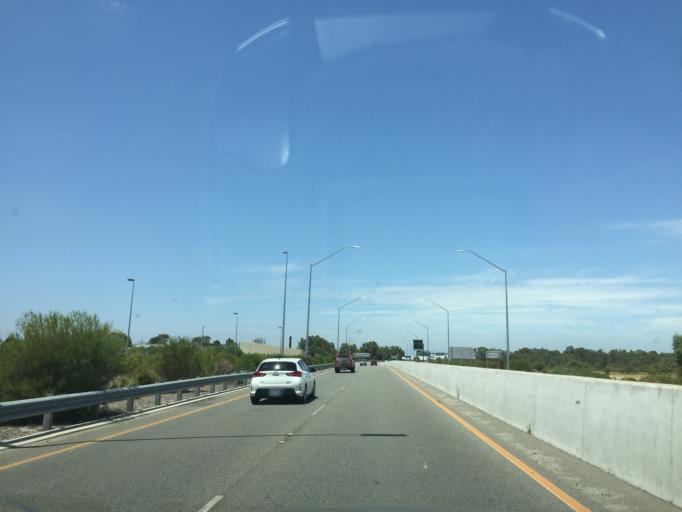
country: AU
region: Western Australia
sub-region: Belmont
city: Kewdale
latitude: -31.9573
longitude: 115.9686
